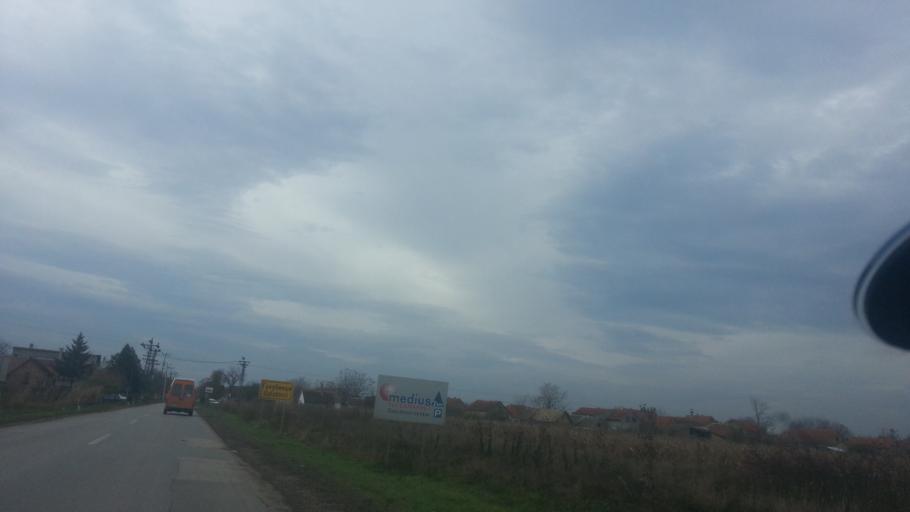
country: RS
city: Golubinci
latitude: 44.9811
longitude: 20.0824
